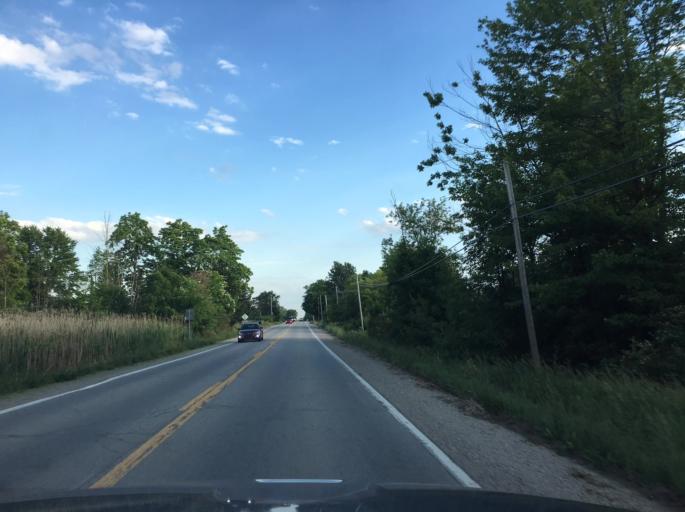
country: US
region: Michigan
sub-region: Macomb County
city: Romeo
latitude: 42.7740
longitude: -82.9615
